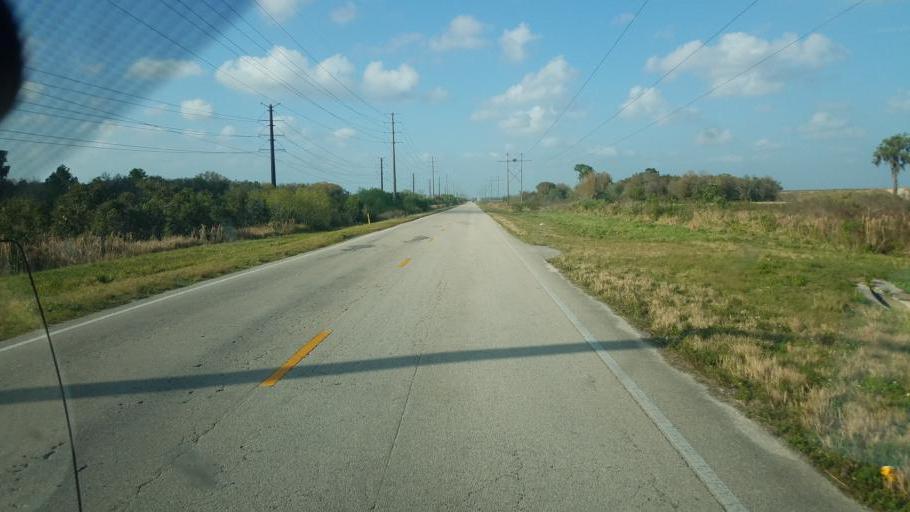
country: US
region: Florida
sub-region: Hardee County
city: Wauchula
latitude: 27.5562
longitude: -81.9326
